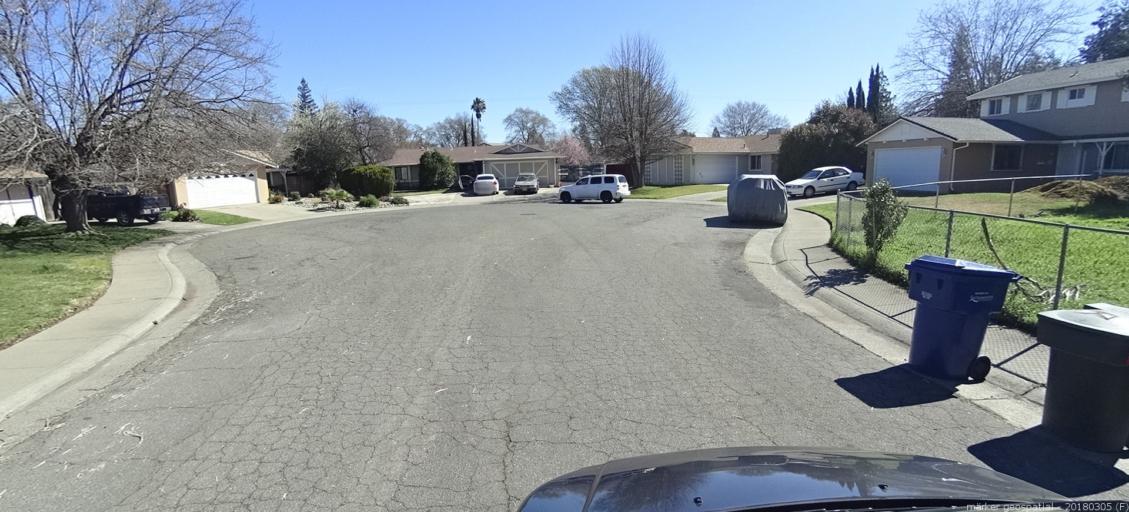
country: US
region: California
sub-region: Sacramento County
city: Florin
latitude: 38.5012
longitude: -121.4167
